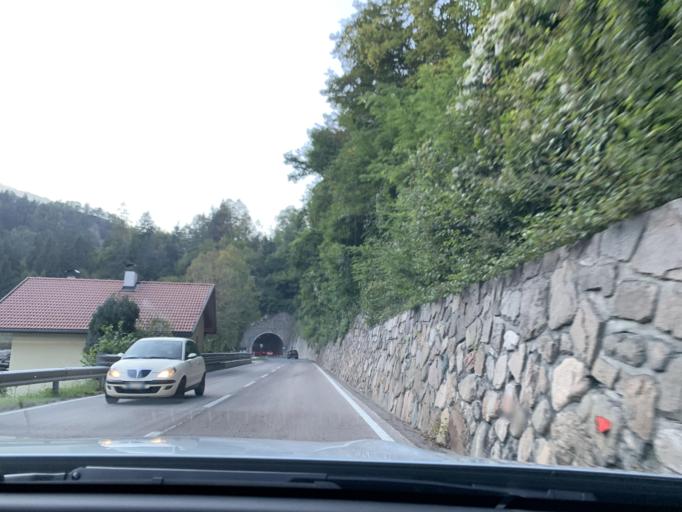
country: IT
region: Trentino-Alto Adige
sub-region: Bolzano
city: Nova Ponente
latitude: 46.4511
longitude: 11.4470
